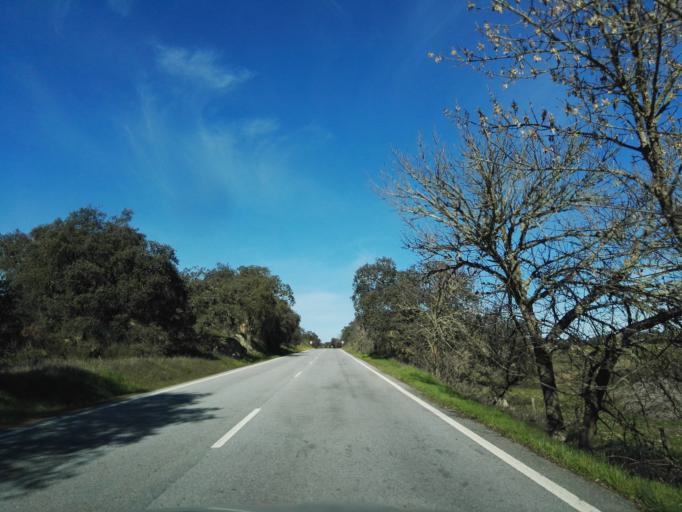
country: PT
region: Portalegre
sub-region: Arronches
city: Arronches
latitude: 39.0719
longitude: -7.2771
